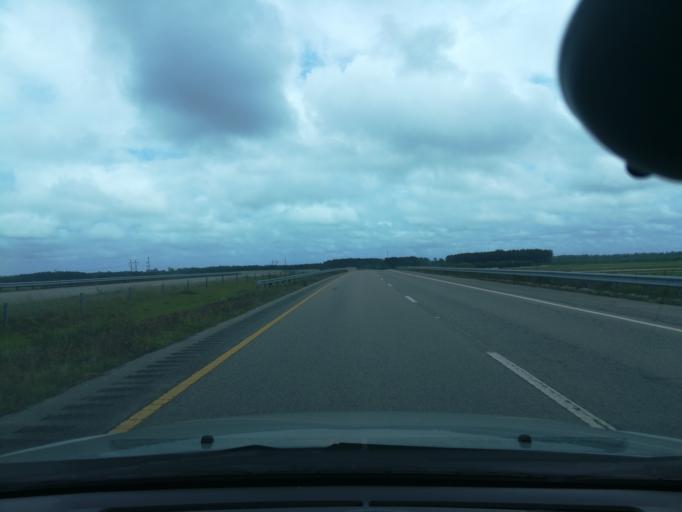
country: US
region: North Carolina
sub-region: Chowan County
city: Edenton
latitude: 35.9069
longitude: -76.4842
